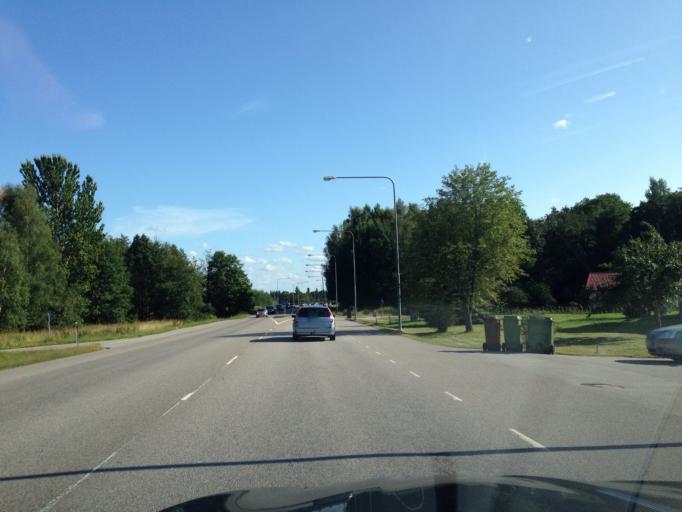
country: SE
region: Vaestra Goetaland
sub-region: Trollhattan
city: Trollhattan
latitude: 58.3114
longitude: 12.2920
